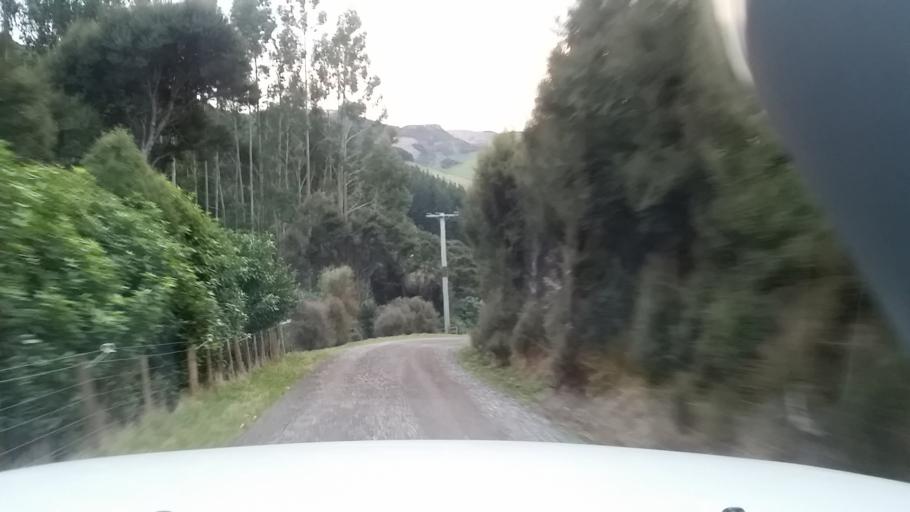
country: NZ
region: Canterbury
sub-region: Christchurch City
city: Christchurch
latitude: -43.7356
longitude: 172.7768
